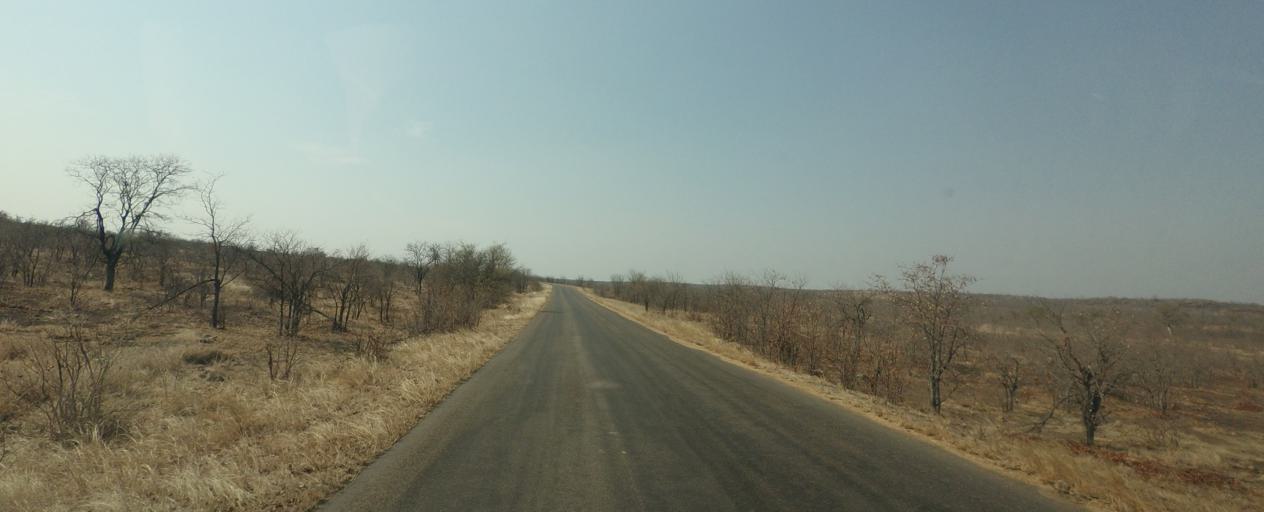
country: ZA
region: Limpopo
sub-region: Mopani District Municipality
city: Phalaborwa
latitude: -23.9841
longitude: 31.6430
